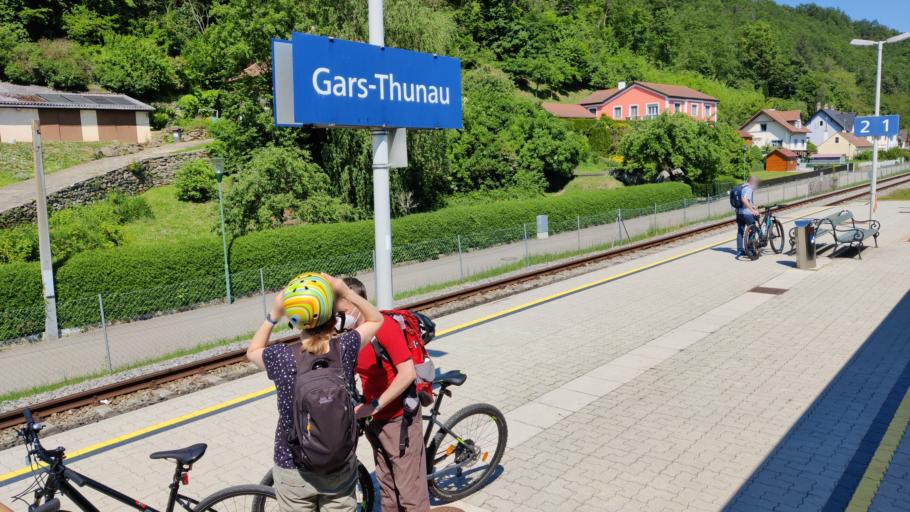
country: AT
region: Lower Austria
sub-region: Politischer Bezirk Horn
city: Gars am Kamp
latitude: 48.5974
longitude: 15.6552
